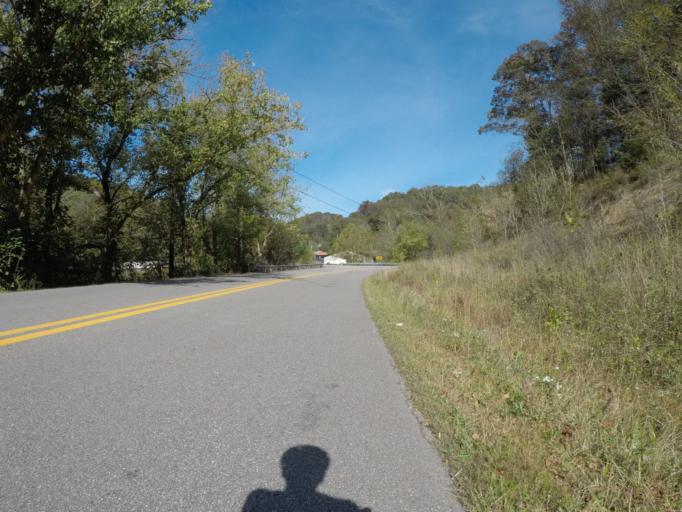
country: US
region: West Virginia
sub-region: Wayne County
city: Lavalette
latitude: 38.3464
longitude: -82.4505
